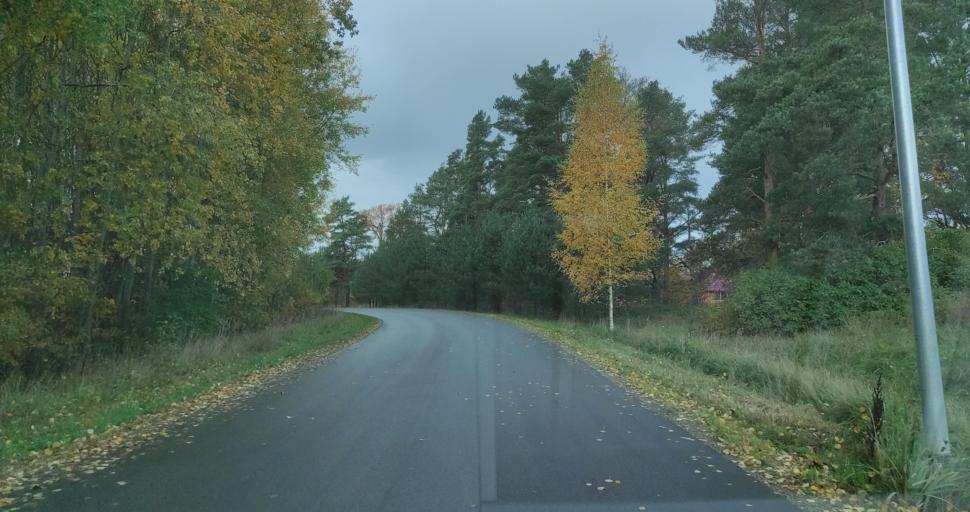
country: LV
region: Skrunda
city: Skrunda
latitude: 56.6842
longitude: 22.0095
